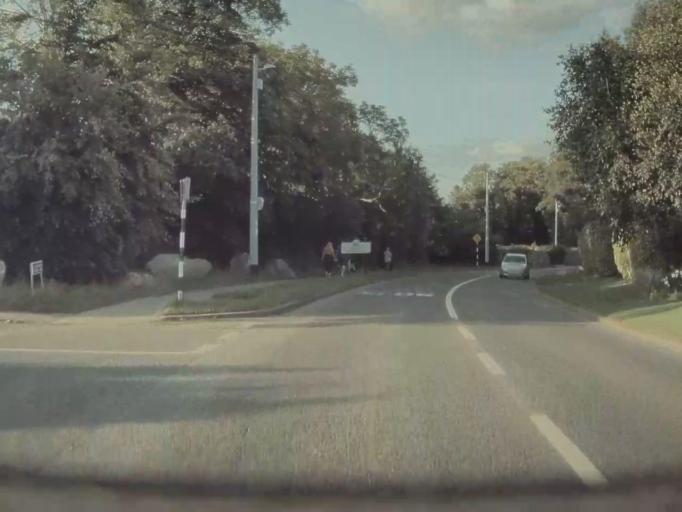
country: IE
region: Leinster
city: Sandyford
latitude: 53.2564
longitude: -6.2156
